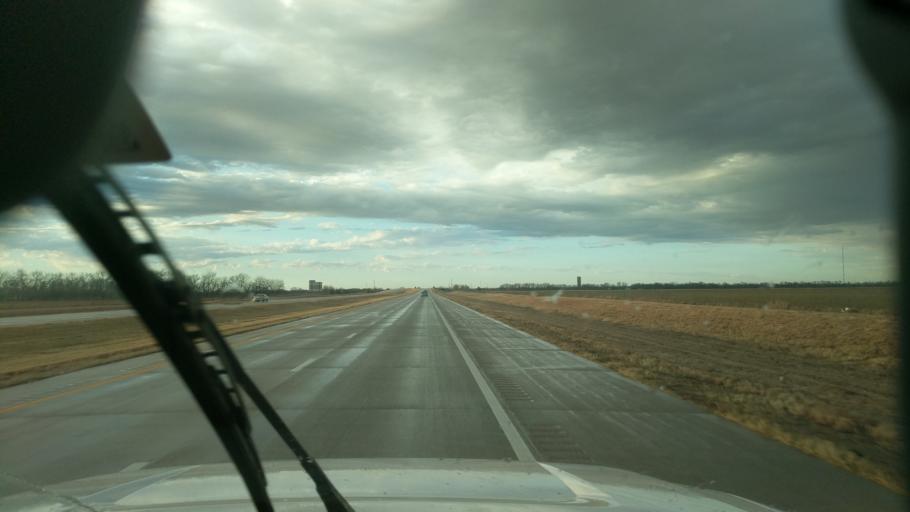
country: US
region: Kansas
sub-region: Harvey County
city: North Newton
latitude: 38.0959
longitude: -97.3646
